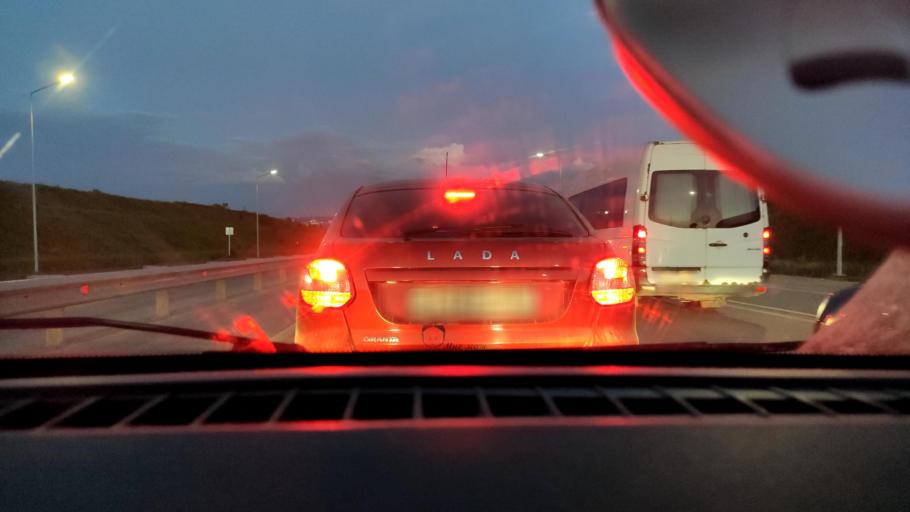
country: RU
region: Perm
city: Polazna
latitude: 58.1956
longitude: 56.4057
